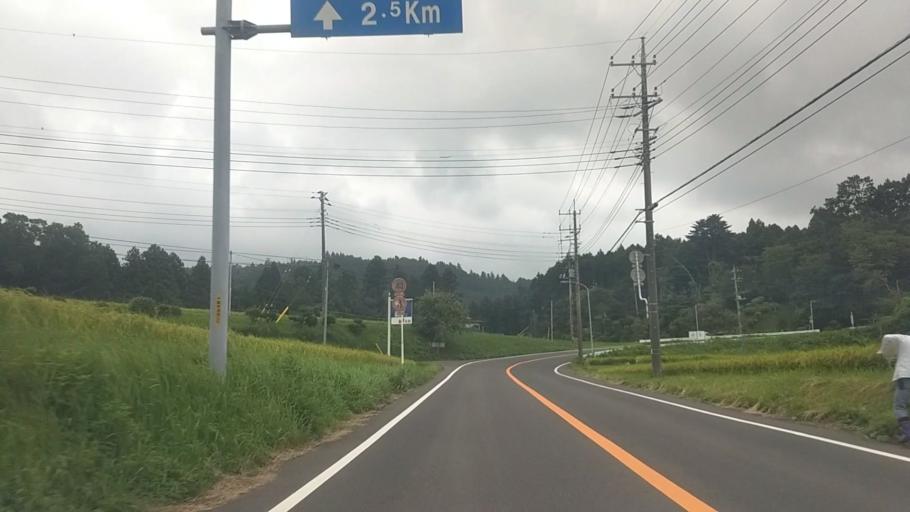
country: JP
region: Chiba
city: Kawaguchi
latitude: 35.2206
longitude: 140.0744
